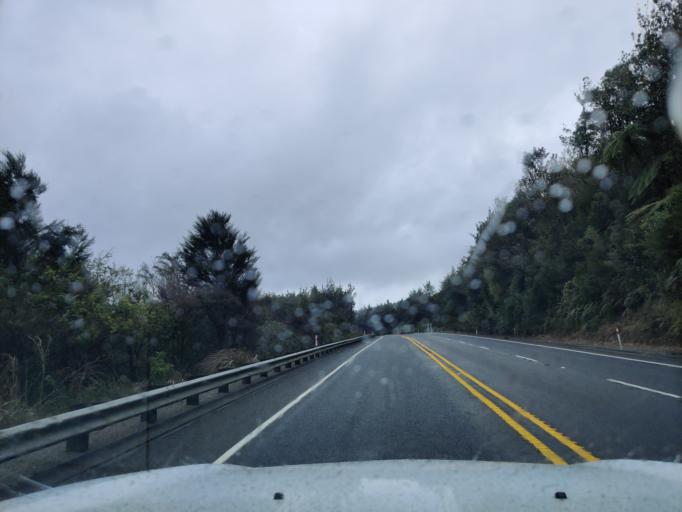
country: NZ
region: Waikato
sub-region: South Waikato District
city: Tokoroa
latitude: -38.0107
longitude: 175.9330
